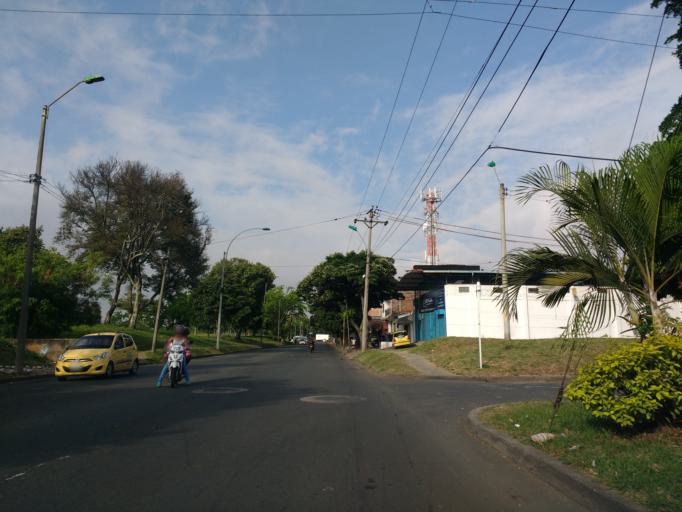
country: CO
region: Valle del Cauca
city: Cali
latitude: 3.4772
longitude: -76.5129
